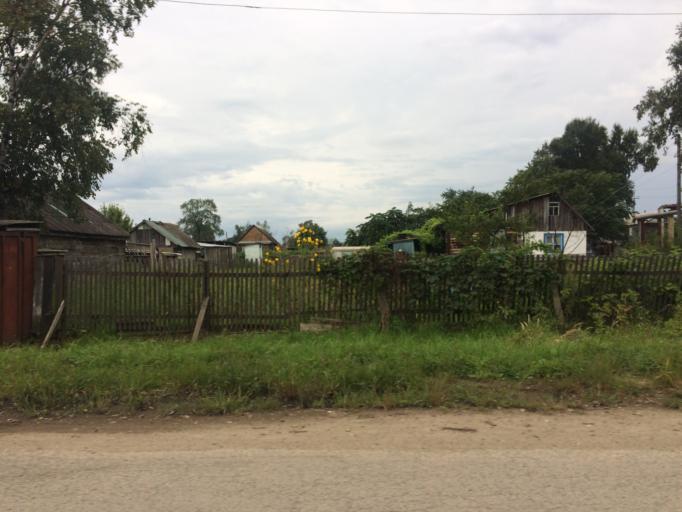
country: RU
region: Primorskiy
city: Dal'nerechensk
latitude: 45.9342
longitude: 133.7455
